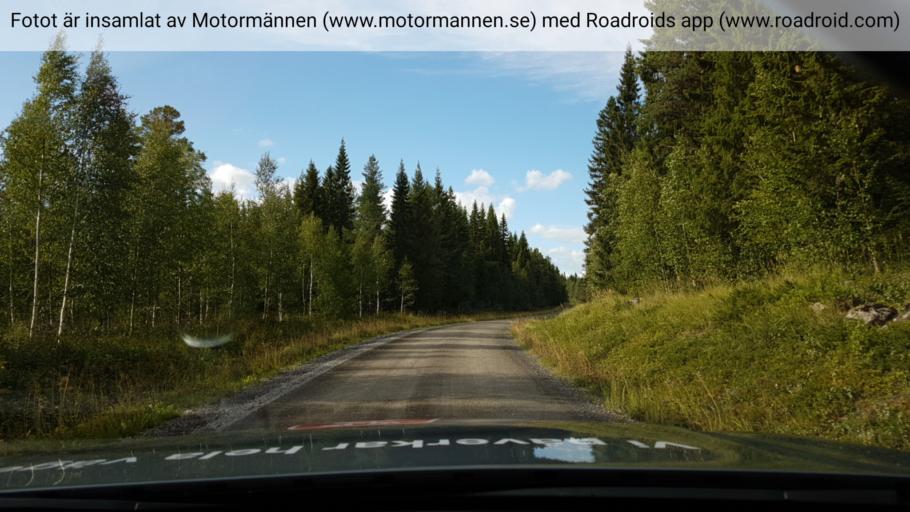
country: SE
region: Jaemtland
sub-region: OEstersunds Kommun
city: Lit
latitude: 63.3119
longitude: 15.2400
